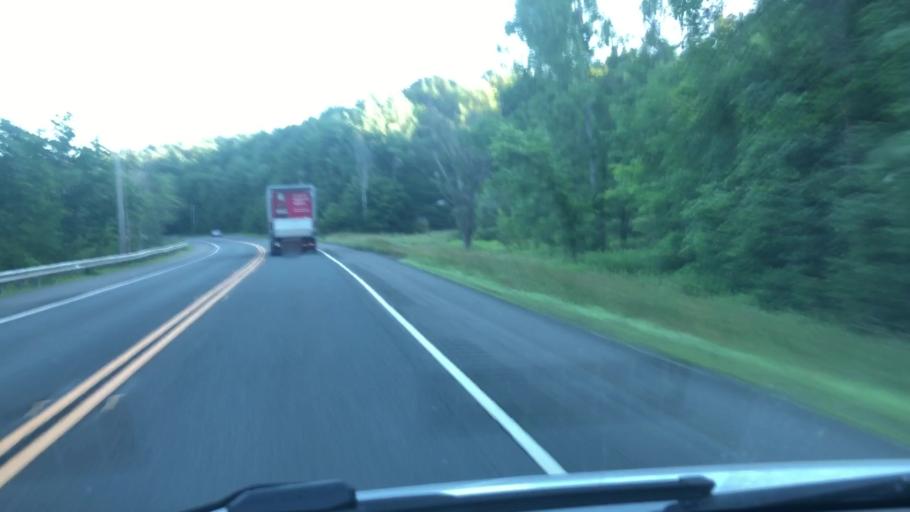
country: US
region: Massachusetts
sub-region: Hampshire County
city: Chesterfield
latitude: 42.4437
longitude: -72.8694
